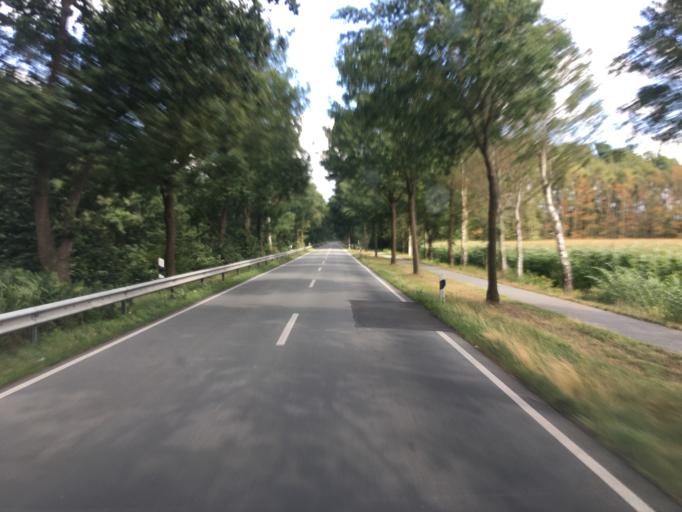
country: DE
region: Lower Saxony
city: Friesoythe
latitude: 53.0847
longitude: 7.8145
